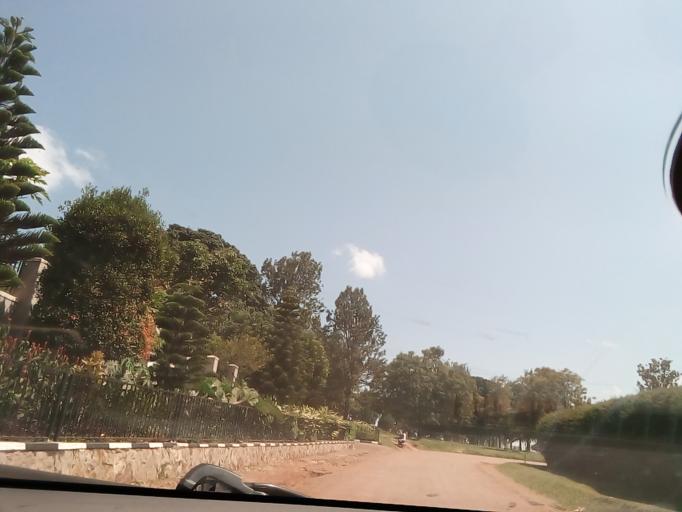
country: UG
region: Central Region
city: Masaka
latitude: -0.3323
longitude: 31.7398
